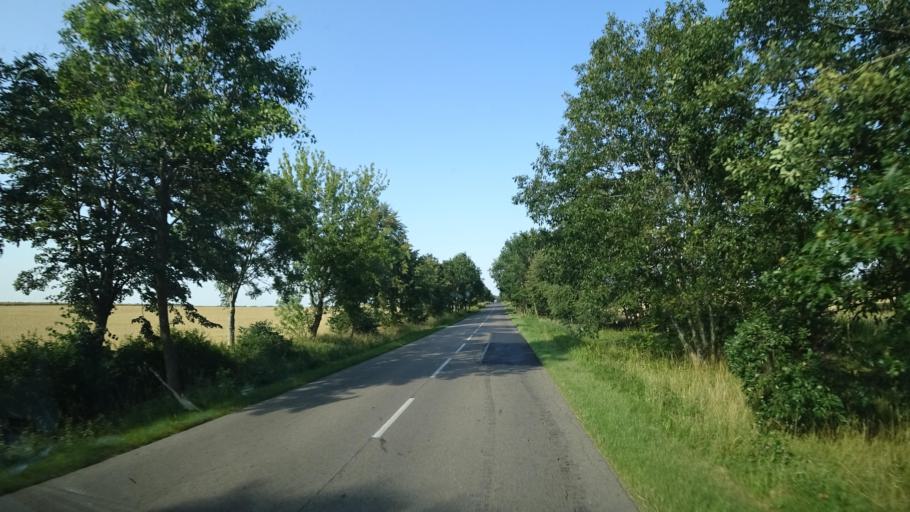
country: PL
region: Pomeranian Voivodeship
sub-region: Powiat czluchowski
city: Przechlewo
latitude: 53.8146
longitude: 17.3593
